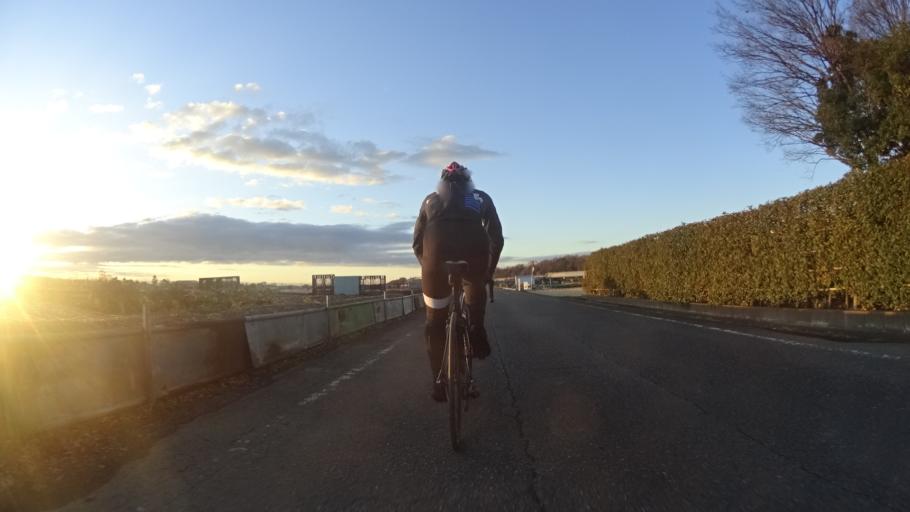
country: JP
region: Kanagawa
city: Zama
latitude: 35.5137
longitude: 139.3683
